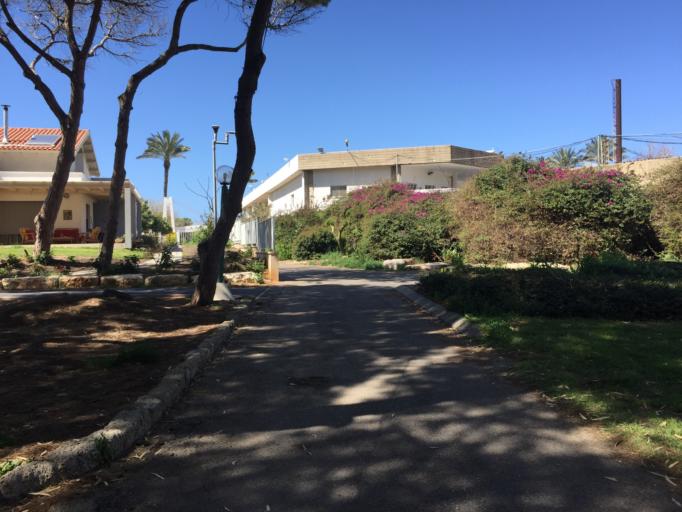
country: IL
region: Haifa
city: Qesarya
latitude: 32.4930
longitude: 34.8917
